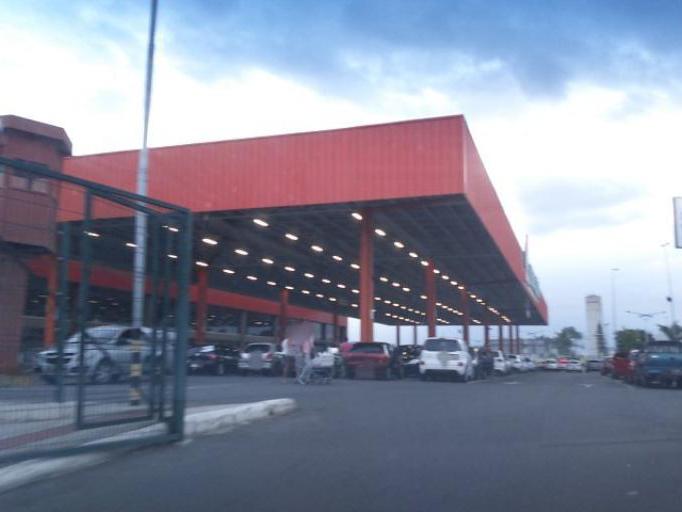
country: BR
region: Santa Catarina
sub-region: Itajai
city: Itajai
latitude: -26.9125
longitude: -48.6890
